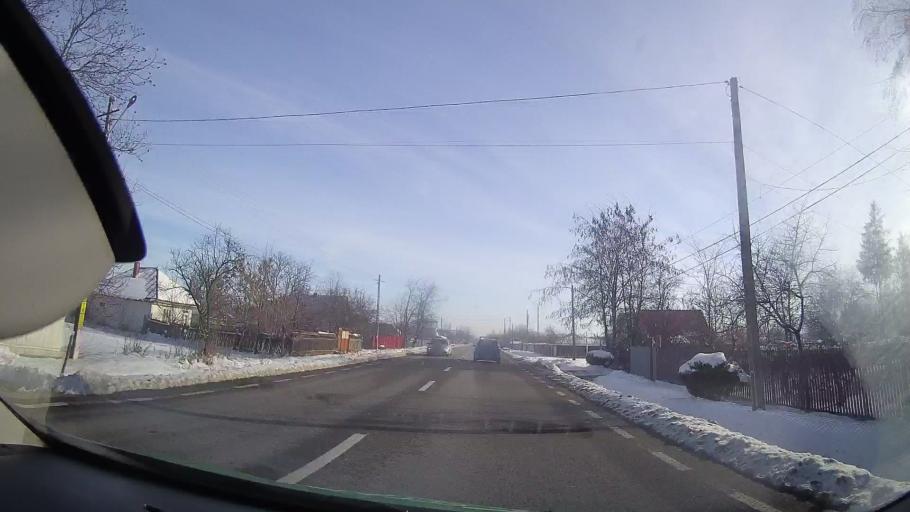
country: RO
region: Neamt
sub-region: Comuna Negresti
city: Negresti
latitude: 47.0573
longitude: 26.3915
